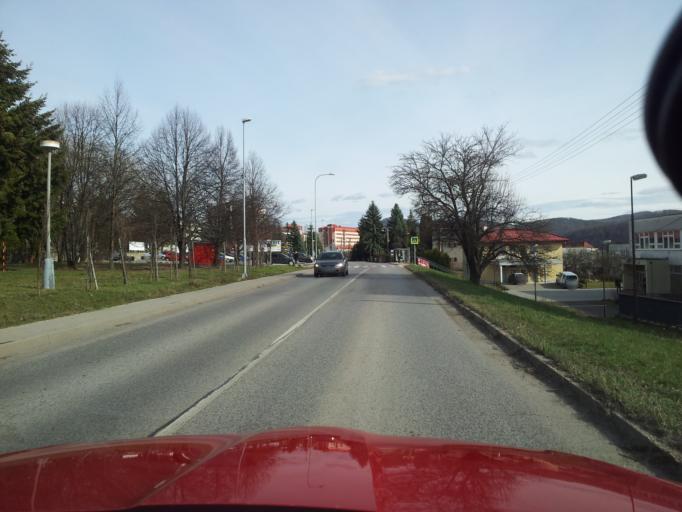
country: SK
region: Banskobystricky
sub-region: Okres Banska Bystrica
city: Banska Bystrica
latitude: 48.7414
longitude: 19.1209
